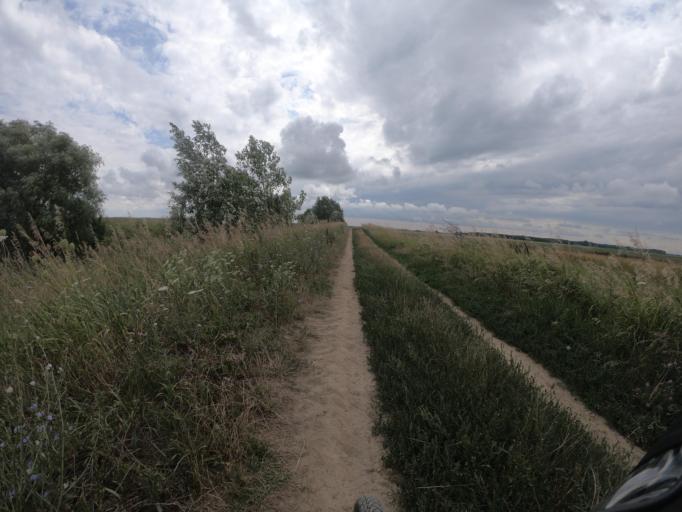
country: HU
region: Jasz-Nagykun-Szolnok
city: Tiszafured
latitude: 47.7192
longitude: 20.7875
